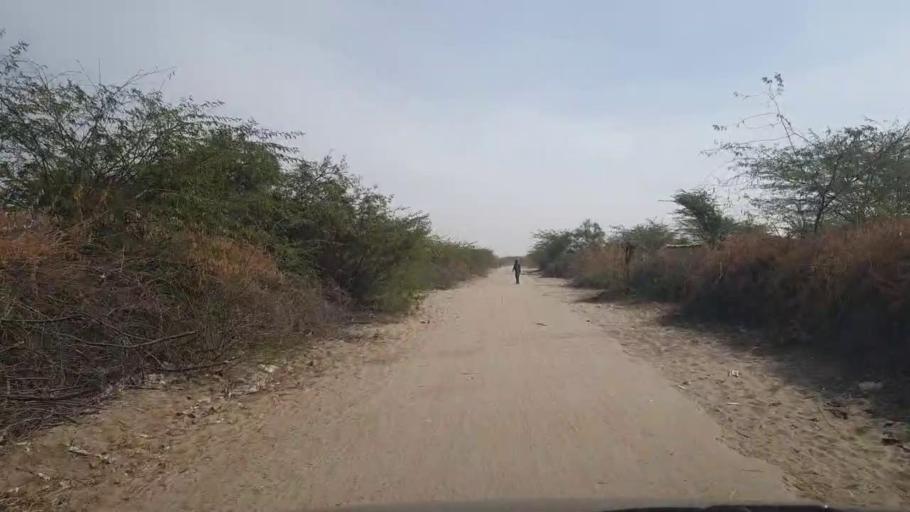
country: PK
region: Sindh
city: Umarkot
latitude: 25.2901
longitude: 69.7197
